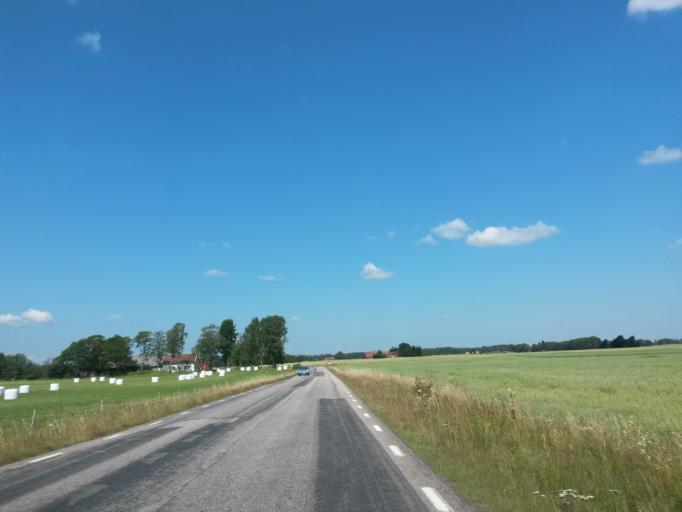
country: SE
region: Vaestra Goetaland
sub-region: Essunga Kommun
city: Nossebro
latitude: 58.1387
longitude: 12.7731
